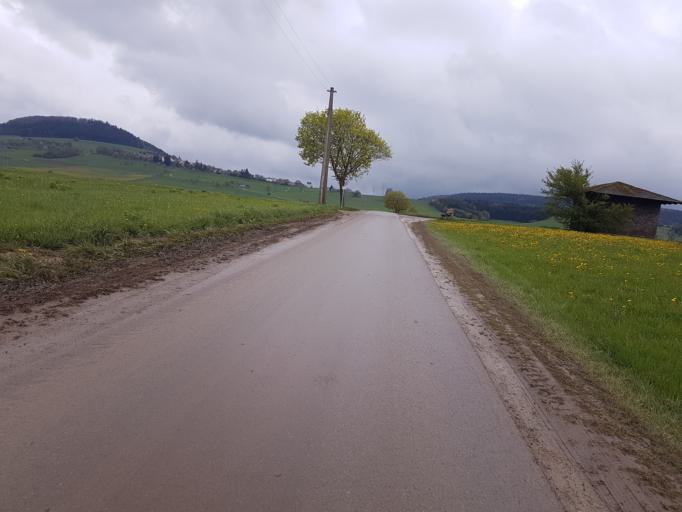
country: DE
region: Baden-Wuerttemberg
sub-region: Freiburg Region
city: Hufingen
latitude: 47.9020
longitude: 8.5395
